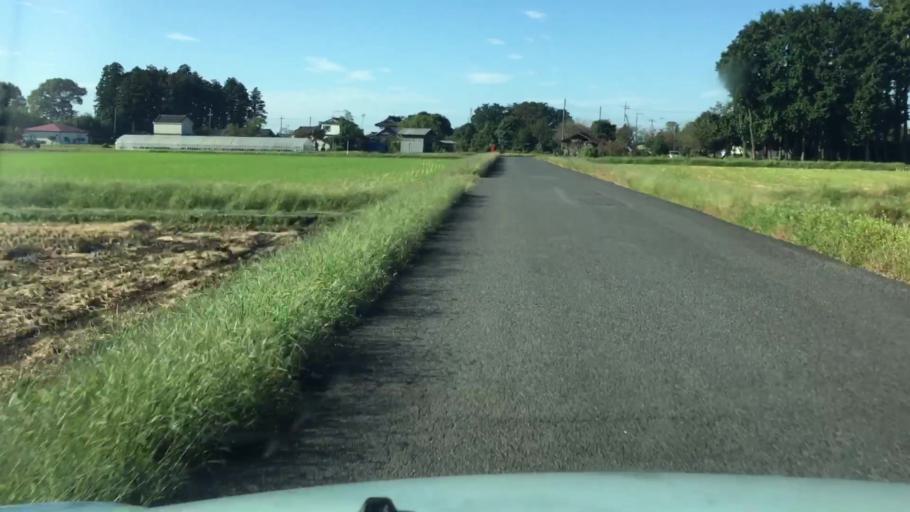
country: JP
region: Tochigi
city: Ujiie
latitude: 36.6938
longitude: 140.0091
